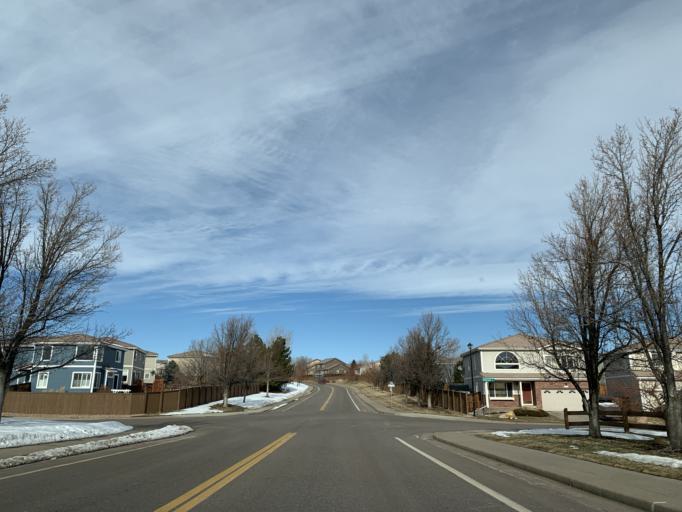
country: US
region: Colorado
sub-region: Douglas County
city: Carriage Club
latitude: 39.5305
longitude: -104.9341
